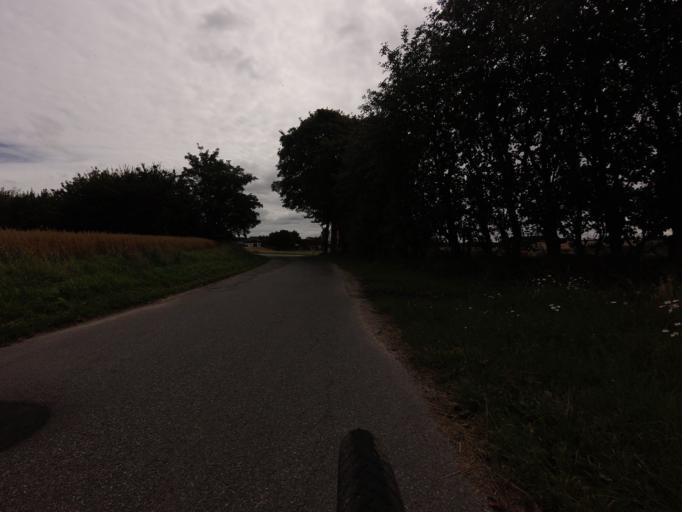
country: DK
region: Central Jutland
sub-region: Syddjurs Kommune
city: Ryomgard
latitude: 56.3885
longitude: 10.5537
